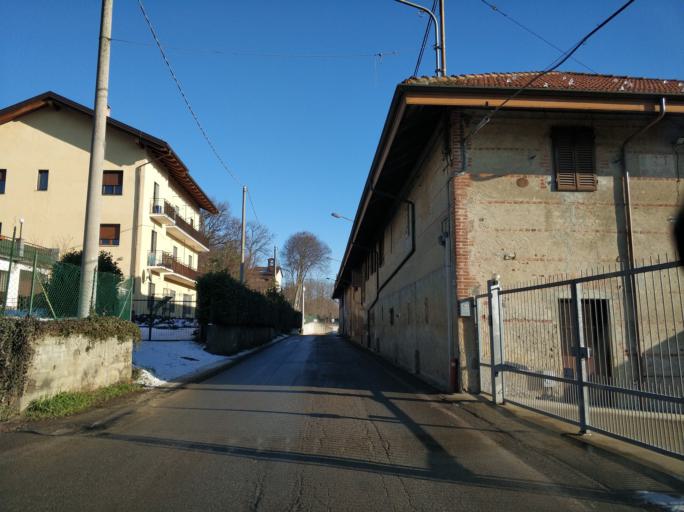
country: IT
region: Piedmont
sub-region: Provincia di Torino
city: San Francesco al Campo
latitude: 45.2175
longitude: 7.6780
